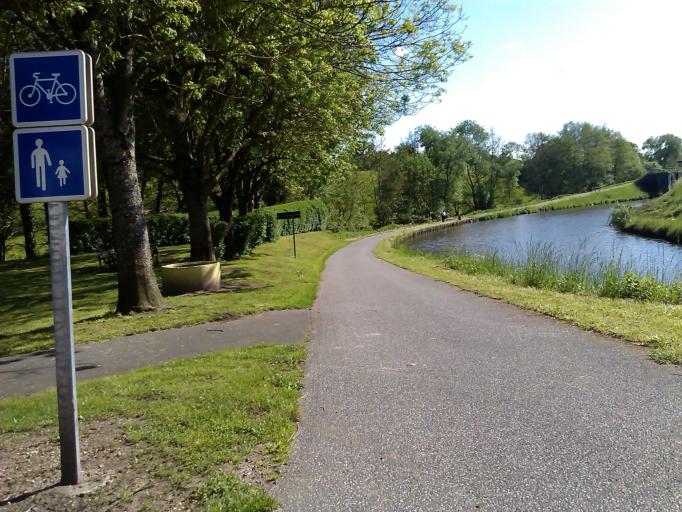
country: FR
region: Bourgogne
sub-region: Departement de Saone-et-Loire
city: Ecuisses
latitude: 46.7731
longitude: 4.5439
